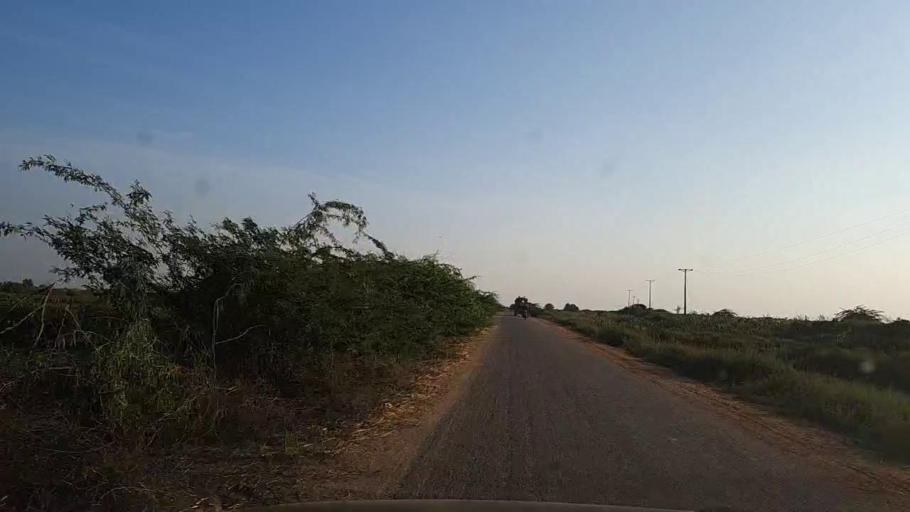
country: PK
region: Sindh
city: Thatta
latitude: 24.6388
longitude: 67.9125
